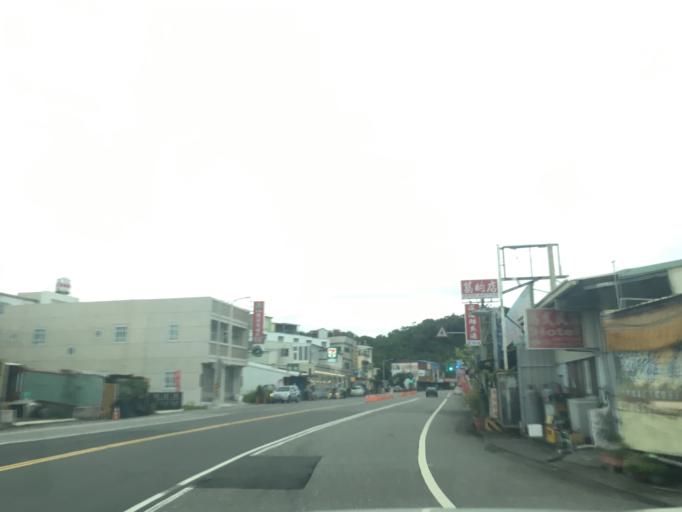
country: TW
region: Taiwan
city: Hengchun
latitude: 22.3389
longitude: 120.8932
